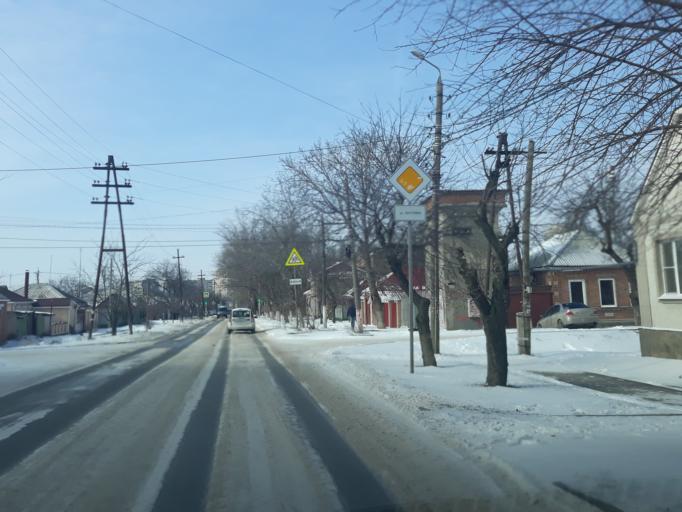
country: RU
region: Rostov
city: Taganrog
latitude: 47.2254
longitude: 38.8819
